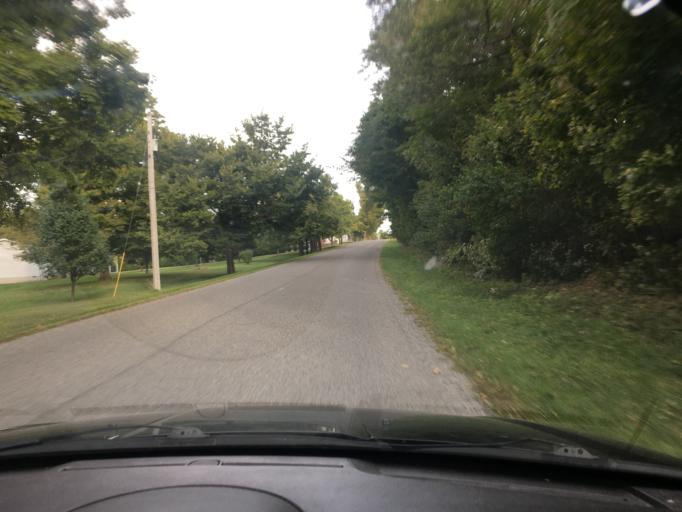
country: US
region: Ohio
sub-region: Logan County
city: West Liberty
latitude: 40.3021
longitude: -83.6955
